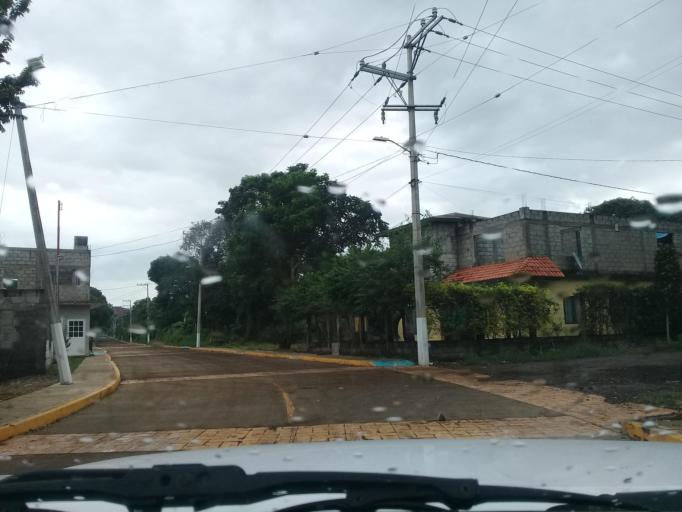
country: MX
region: Veracruz
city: San Andres Tuxtla
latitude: 18.4336
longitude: -95.2094
